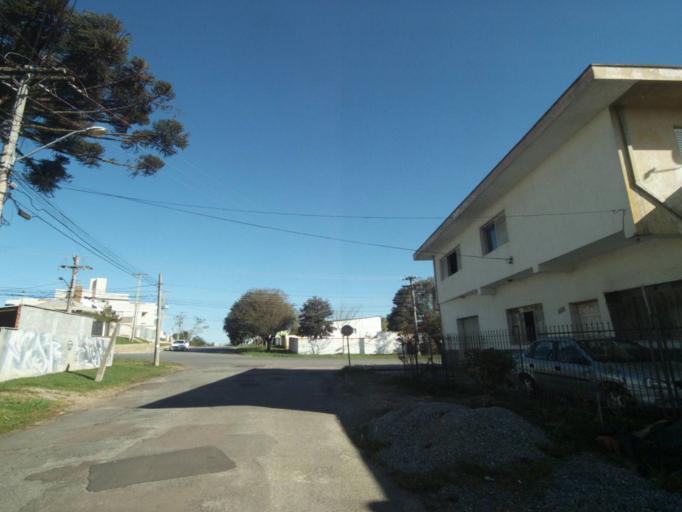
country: BR
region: Parana
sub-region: Curitiba
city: Curitiba
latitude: -25.3899
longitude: -49.2565
